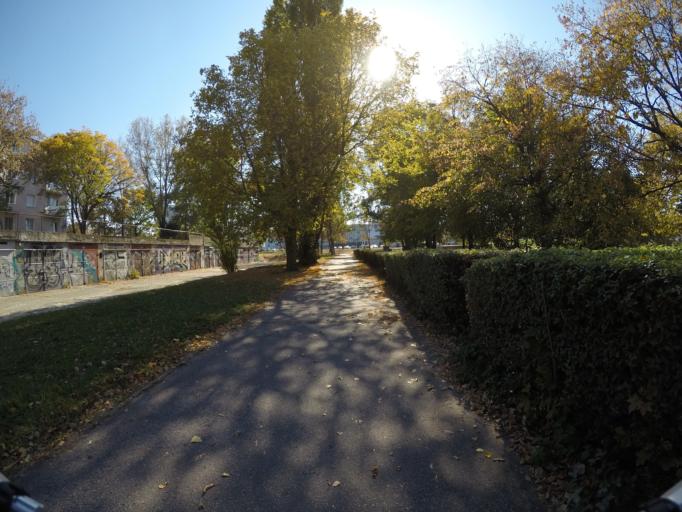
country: SK
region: Bratislavsky
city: Bratislava
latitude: 48.1574
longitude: 17.1492
